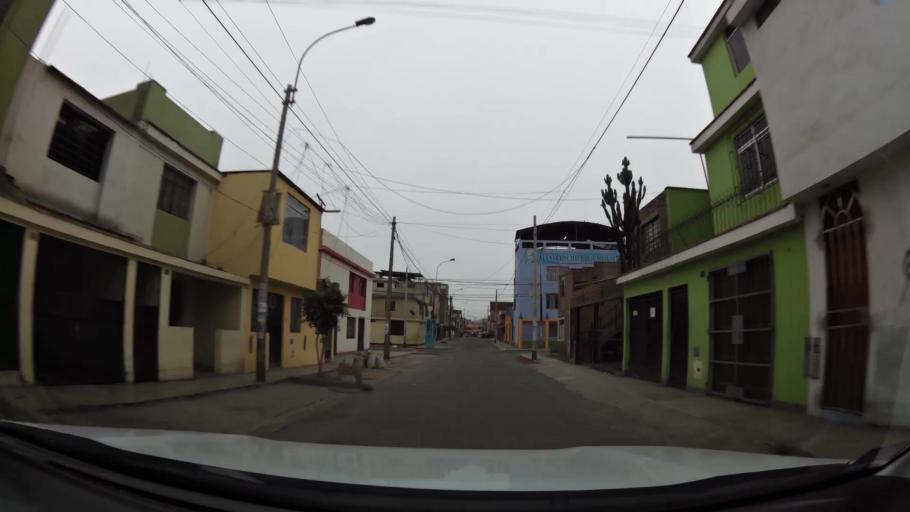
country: PE
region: Lima
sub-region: Lima
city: Surco
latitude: -12.1682
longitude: -76.9752
